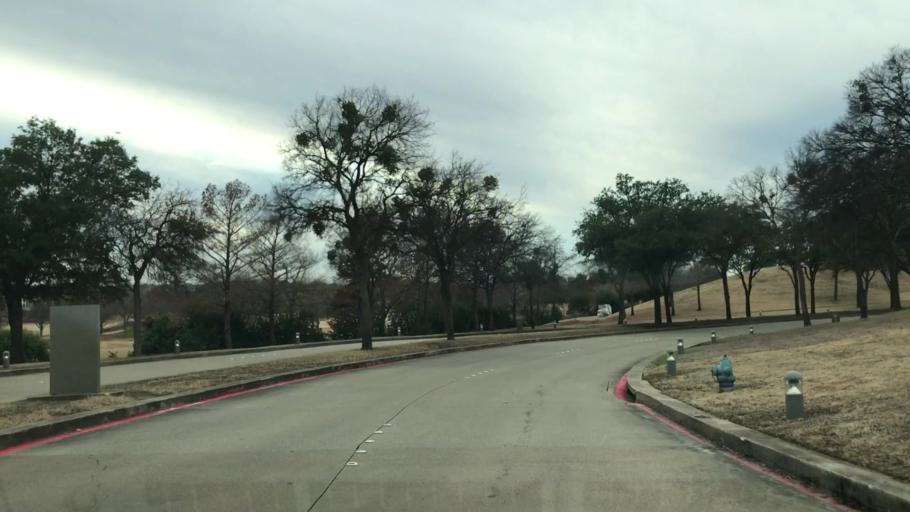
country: US
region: Texas
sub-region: Dallas County
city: Irving
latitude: 32.8757
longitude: -96.9546
